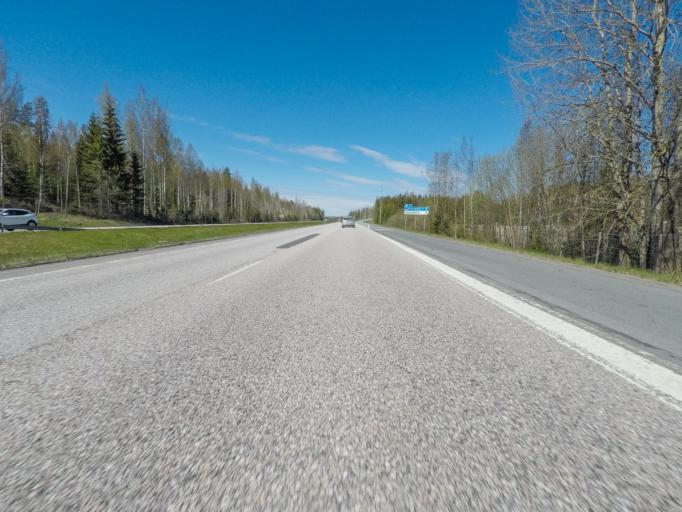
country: FI
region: Uusimaa
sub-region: Helsinki
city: Hyvinge
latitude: 60.6555
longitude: 24.7989
